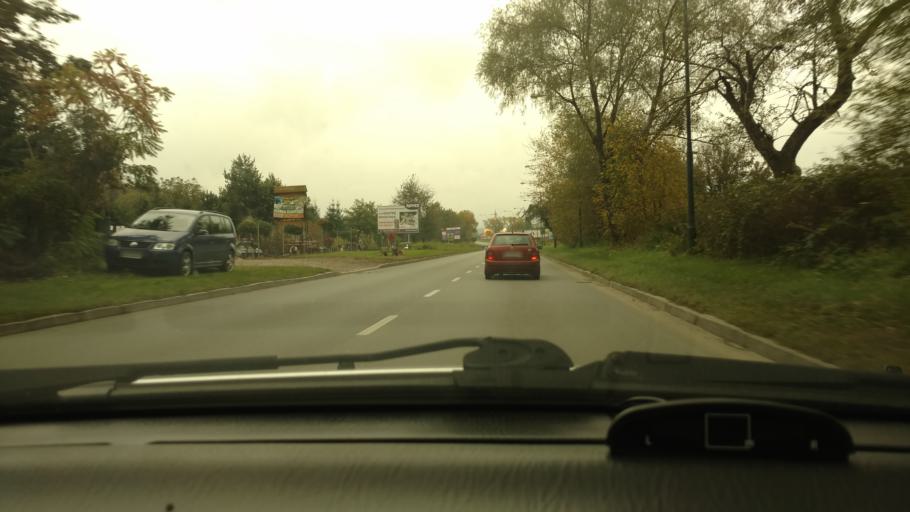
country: PL
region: Lesser Poland Voivodeship
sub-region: Powiat nowosadecki
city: Nowy Sacz
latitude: 49.6350
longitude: 20.7066
